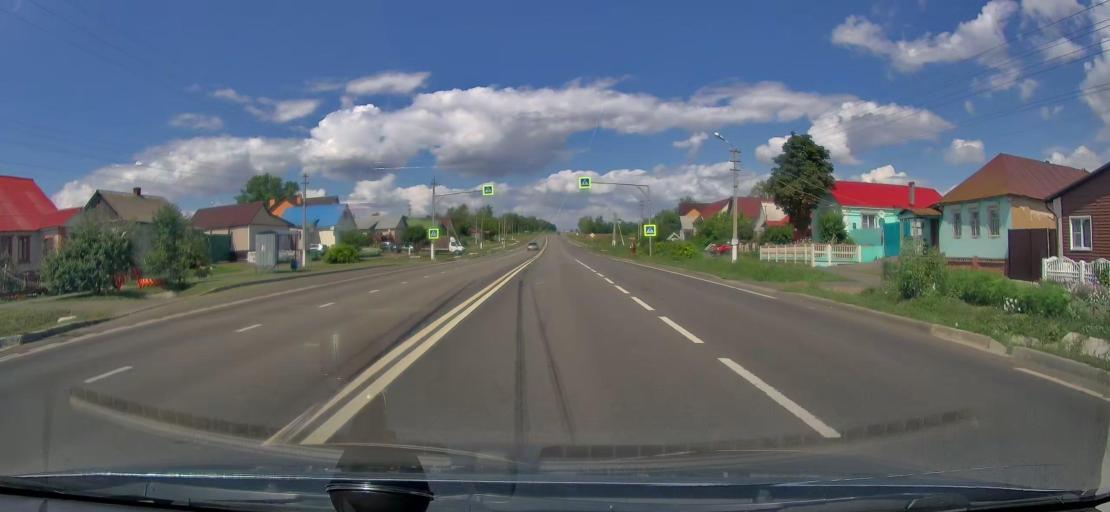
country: RU
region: Kursk
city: Zolotukhino
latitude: 51.9496
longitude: 36.3044
